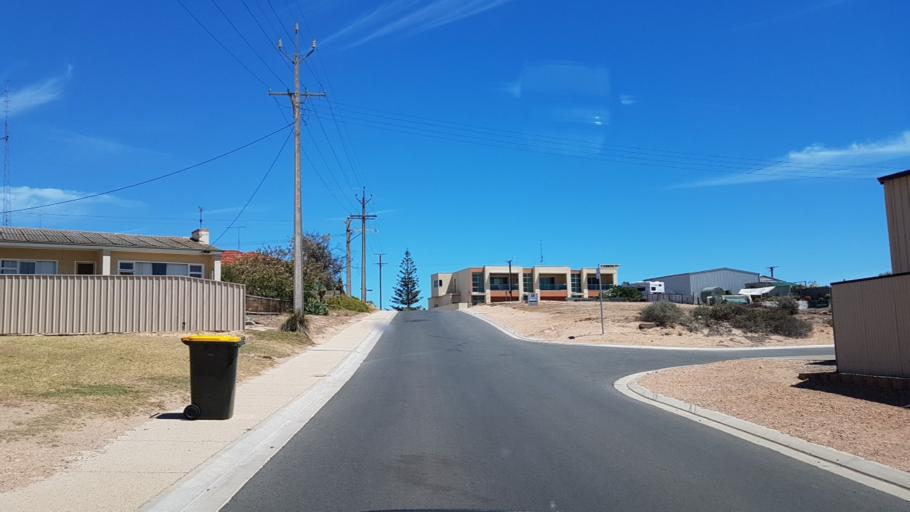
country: AU
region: South Australia
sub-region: Copper Coast
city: Wallaroo
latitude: -34.0555
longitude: 137.5631
